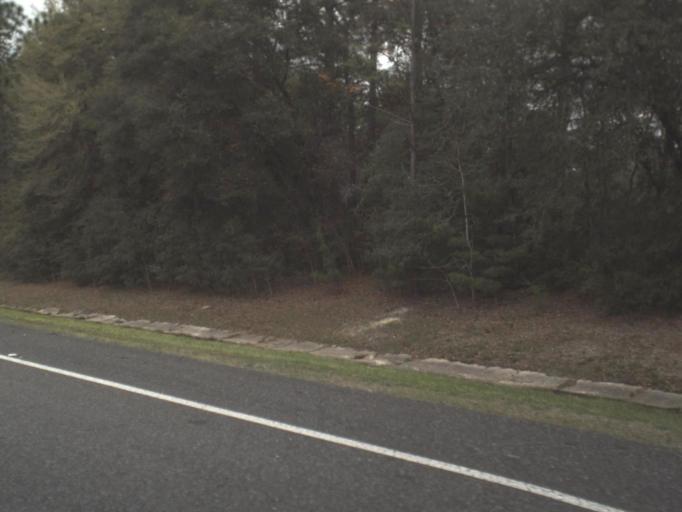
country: US
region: Florida
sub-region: Okaloosa County
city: Crestview
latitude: 30.7271
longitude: -86.5136
